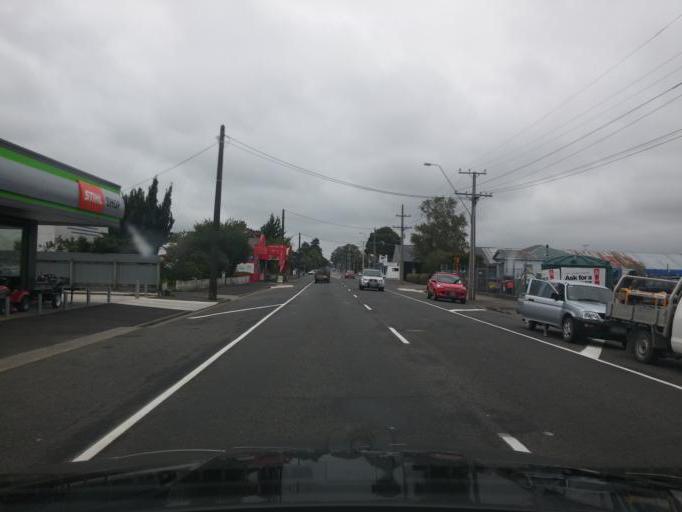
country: NZ
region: Wellington
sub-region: Masterton District
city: Masterton
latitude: -41.0883
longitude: 175.4516
